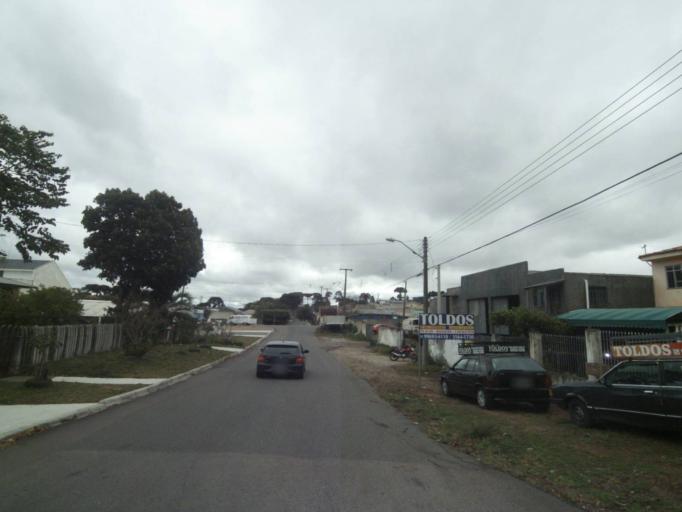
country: BR
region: Parana
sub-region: Sao Jose Dos Pinhais
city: Sao Jose dos Pinhais
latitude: -25.5427
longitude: -49.2989
